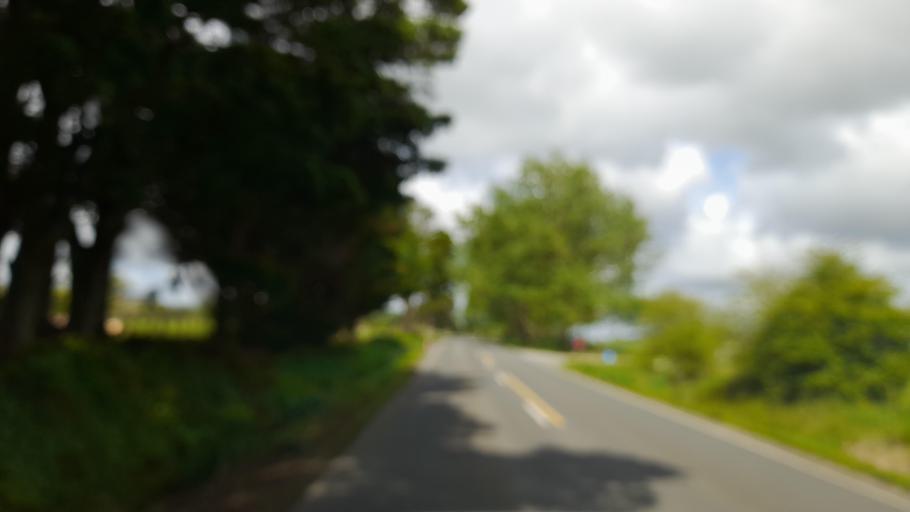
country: NZ
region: Northland
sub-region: Whangarei
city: Maungatapere
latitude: -35.6568
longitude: 174.1615
